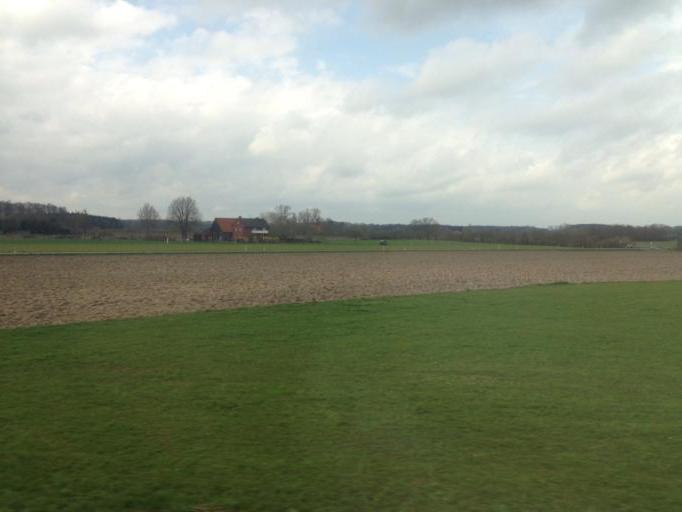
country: DE
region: North Rhine-Westphalia
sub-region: Regierungsbezirk Munster
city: Dulmen
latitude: 51.8564
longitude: 7.3512
